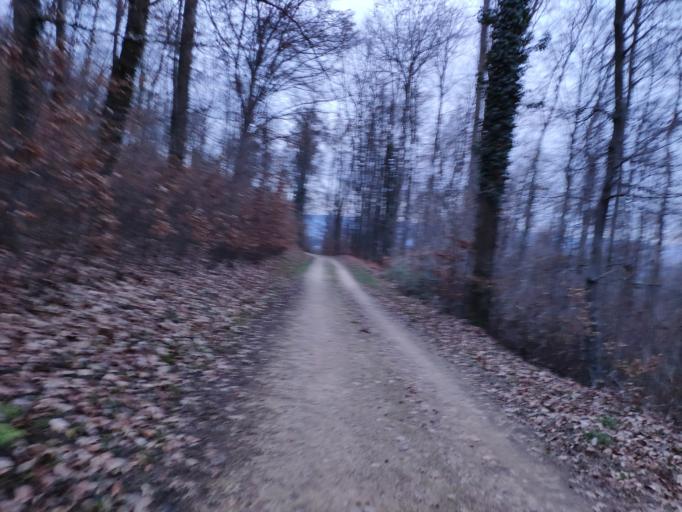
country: DE
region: Baden-Wuerttemberg
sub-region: Freiburg Region
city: Inzlingen
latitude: 47.5942
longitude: 7.6768
